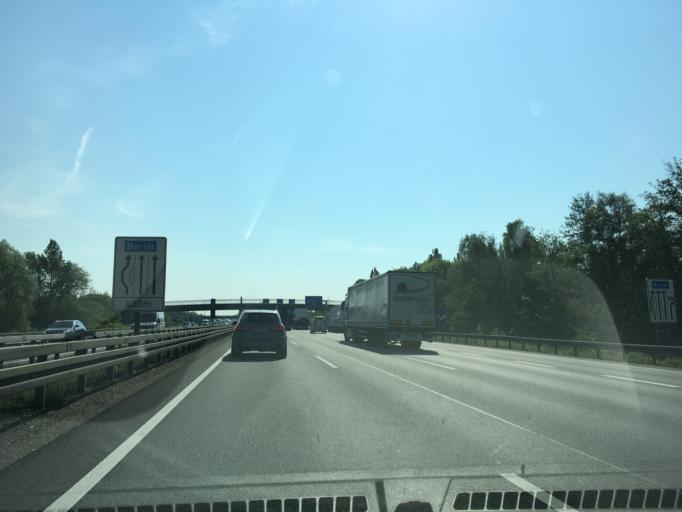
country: DE
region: Lower Saxony
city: Lehrte
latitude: 52.3908
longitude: 9.9534
